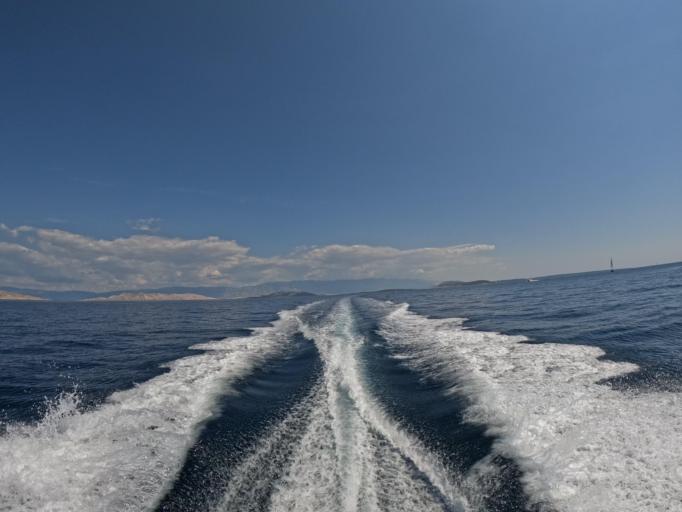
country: HR
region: Primorsko-Goranska
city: Lopar
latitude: 44.8935
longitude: 14.6270
